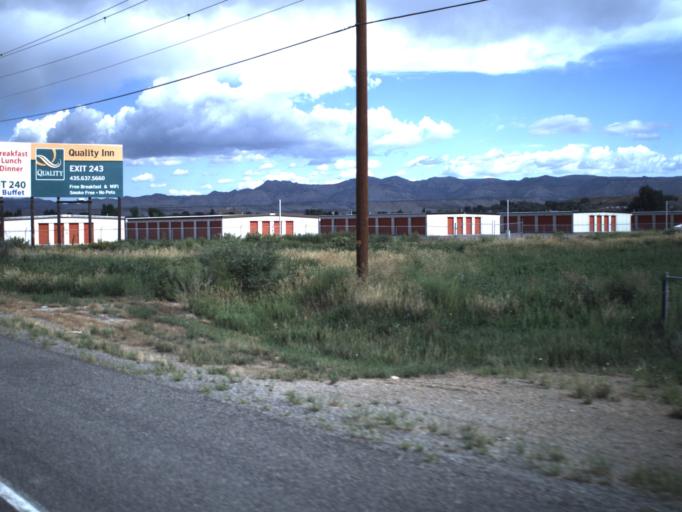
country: US
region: Utah
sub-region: Carbon County
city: Wellington
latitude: 39.5631
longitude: -110.7703
